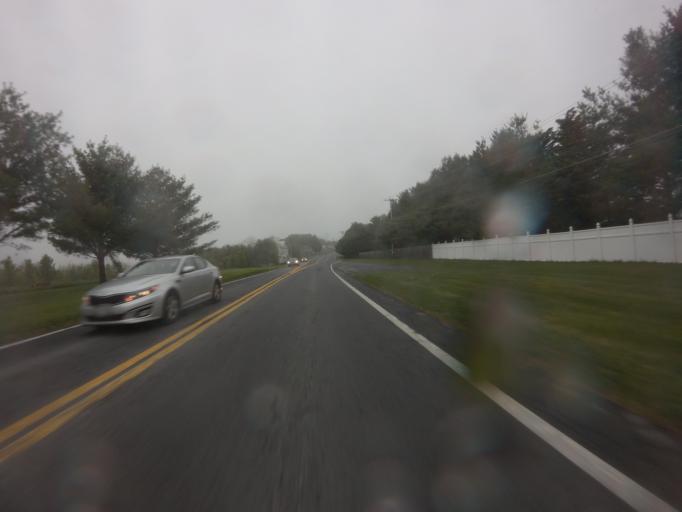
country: US
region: Maryland
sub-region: Carroll County
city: Eldersburg
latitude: 39.4883
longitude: -76.9679
